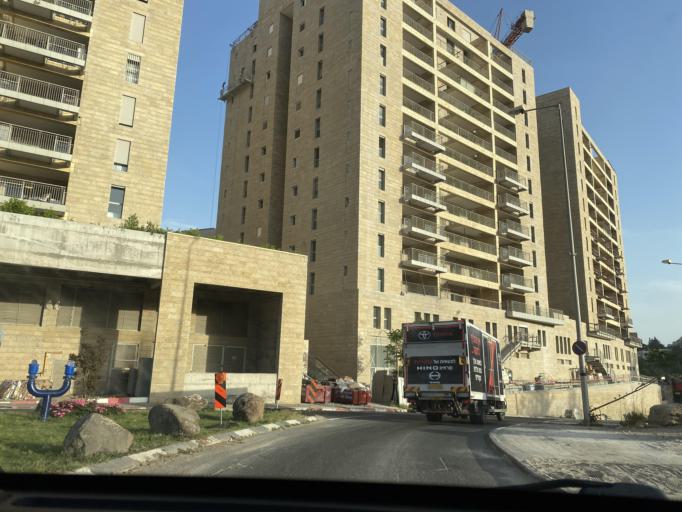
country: IL
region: Jerusalem
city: Jerusalem
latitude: 31.7670
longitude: 35.1931
